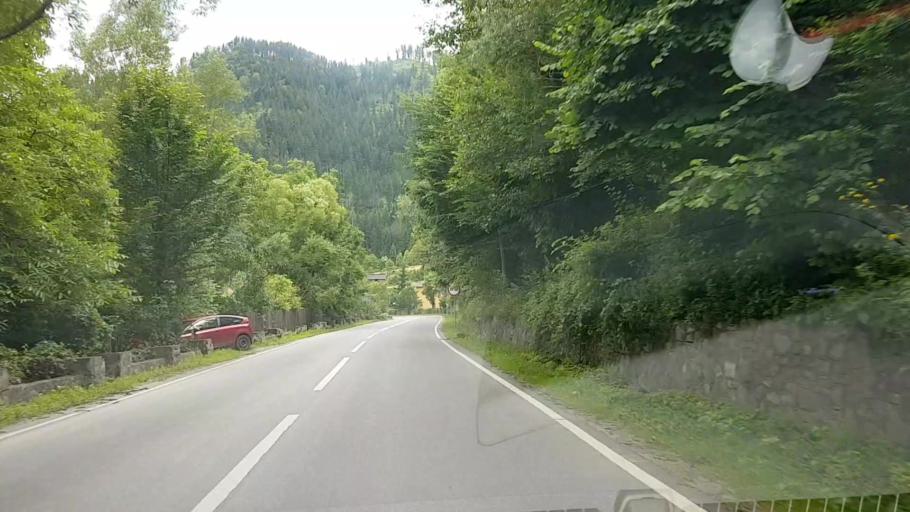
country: RO
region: Neamt
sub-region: Comuna Poiana Teiului
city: Poiana Teiului
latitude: 47.0972
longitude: 25.9419
